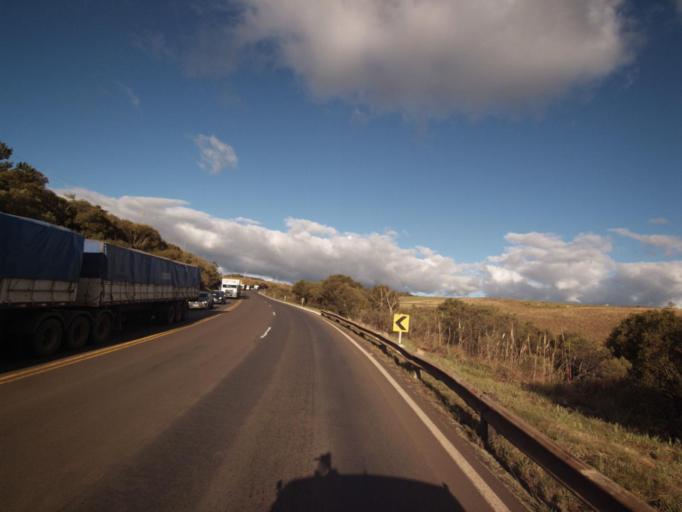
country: BR
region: Santa Catarina
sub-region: Campos Novos
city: Campos Novos
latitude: -27.3344
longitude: -51.3482
